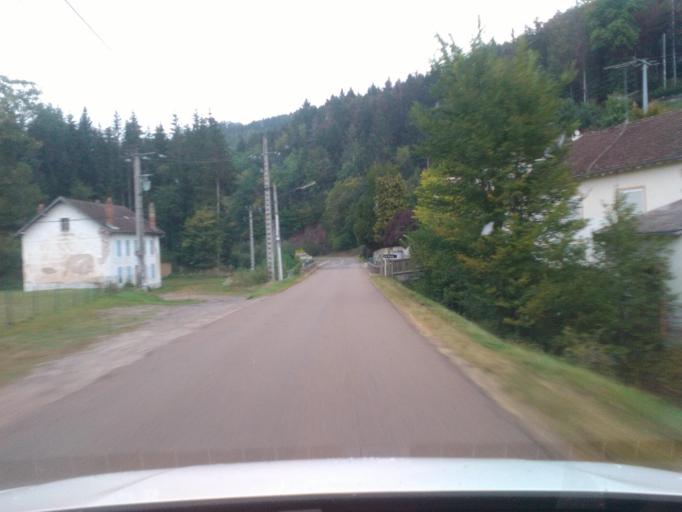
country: FR
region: Lorraine
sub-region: Departement des Vosges
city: Senones
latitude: 48.3376
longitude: 6.9853
